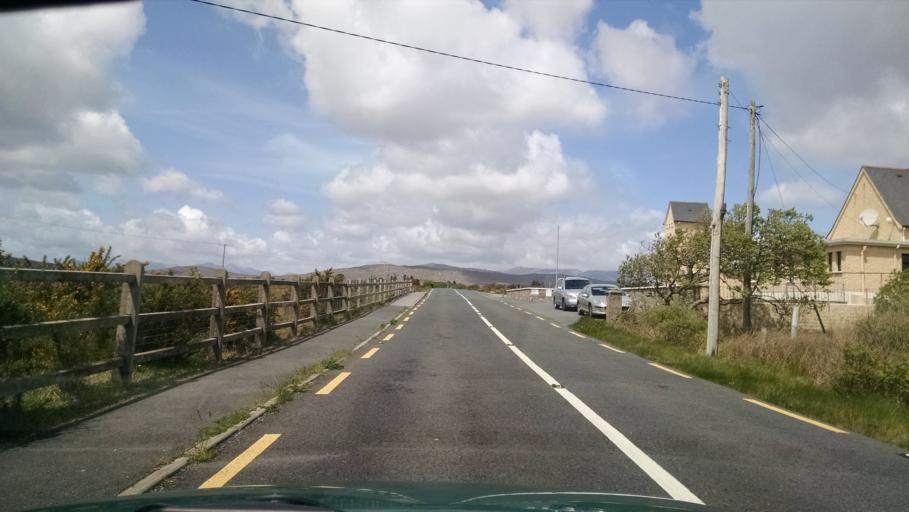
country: IE
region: Connaught
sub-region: County Galway
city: Oughterard
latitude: 53.3770
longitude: -9.5468
